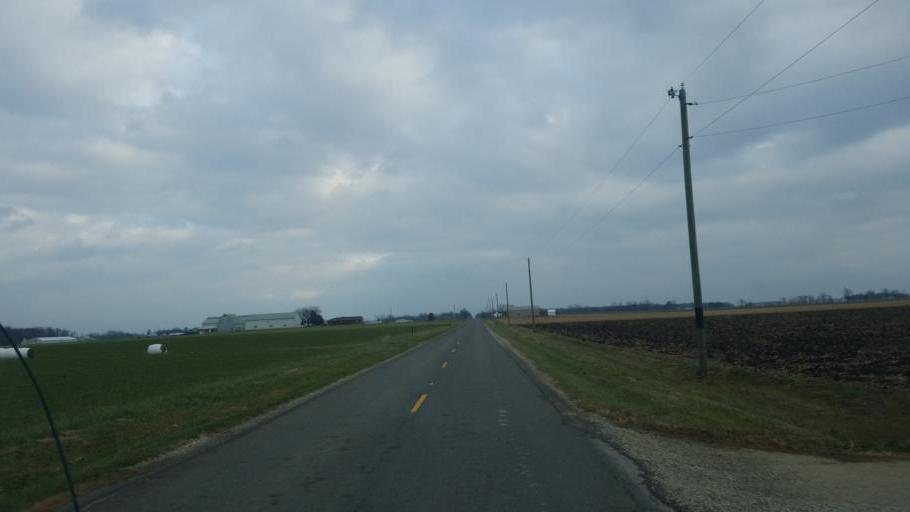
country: US
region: Ohio
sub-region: Mercer County
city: Coldwater
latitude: 40.5089
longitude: -84.6740
